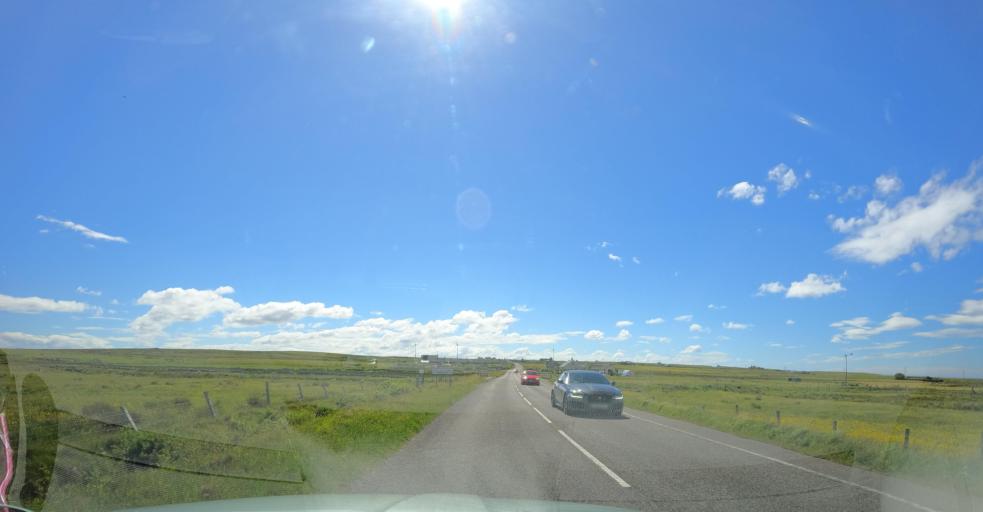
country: GB
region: Scotland
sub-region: Eilean Siar
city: Isle of Lewis
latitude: 58.3951
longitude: -6.4761
